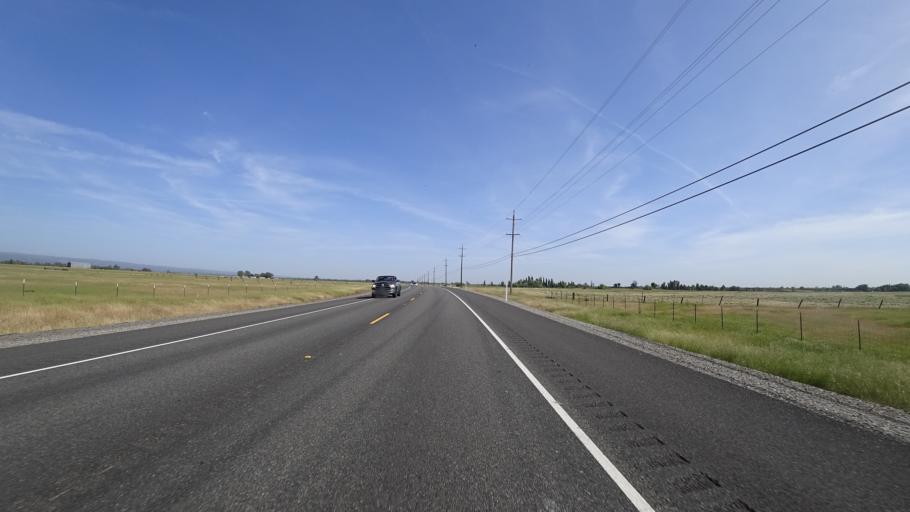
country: US
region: California
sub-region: Glenn County
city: Hamilton City
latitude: 39.8483
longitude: -121.9479
